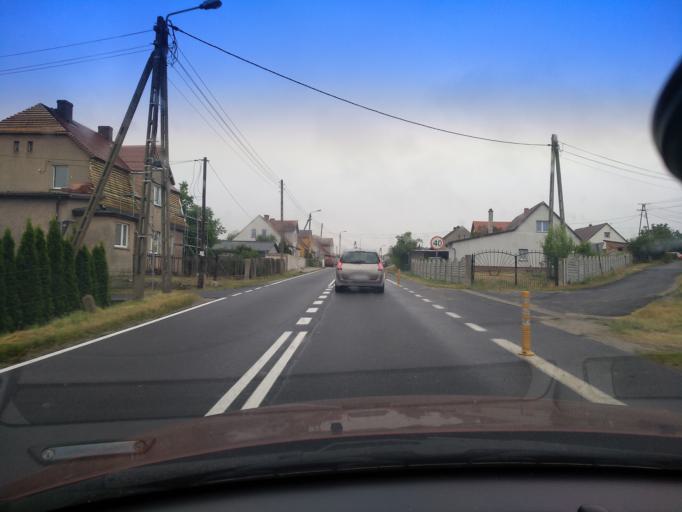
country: PL
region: Lower Silesian Voivodeship
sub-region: Powiat zgorzelecki
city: Wegliniec
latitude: 51.2505
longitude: 15.2208
